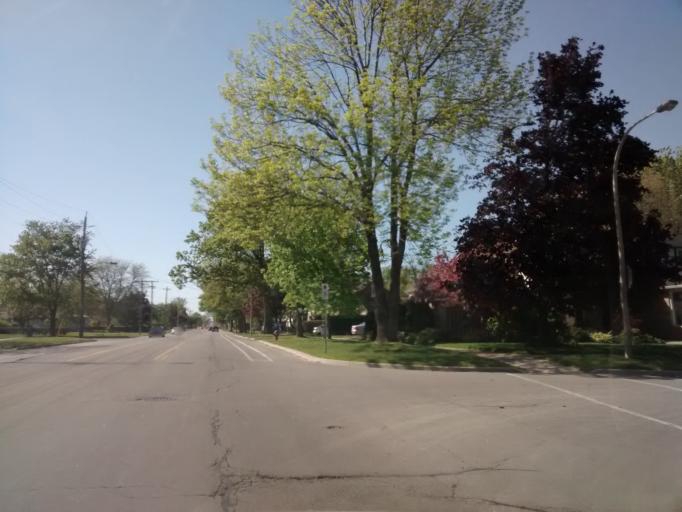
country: CA
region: Ontario
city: Burlington
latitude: 43.3639
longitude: -79.7492
